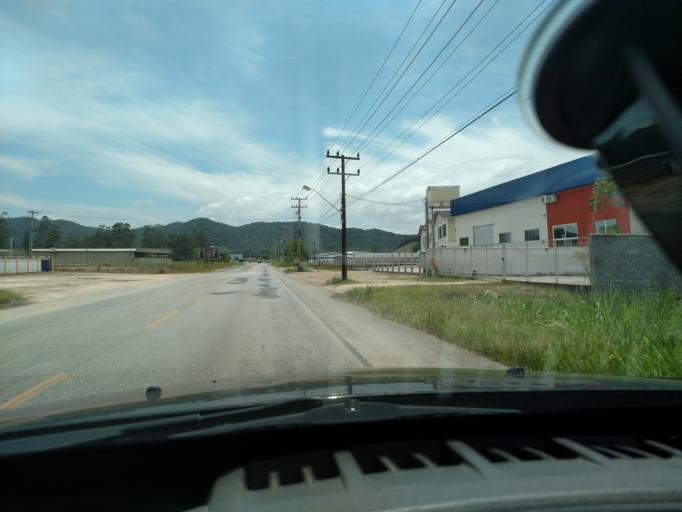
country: BR
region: Santa Catarina
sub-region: Gaspar
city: Gaspar
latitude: -26.9163
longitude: -48.9339
